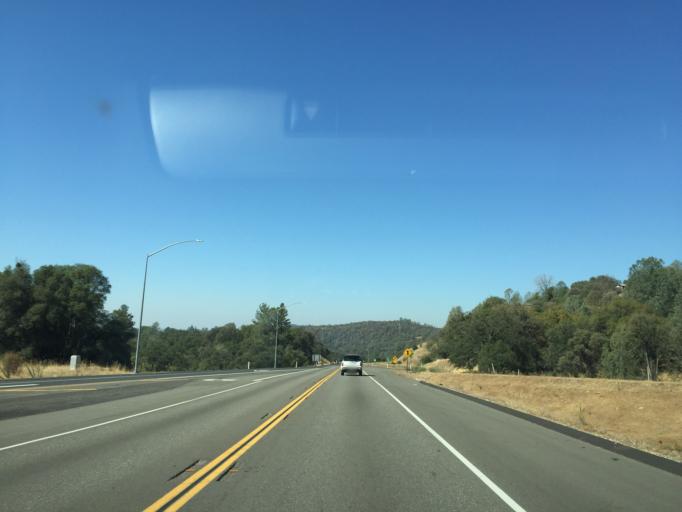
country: US
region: California
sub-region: Tuolumne County
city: East Sonora
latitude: 37.9807
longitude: -120.3205
